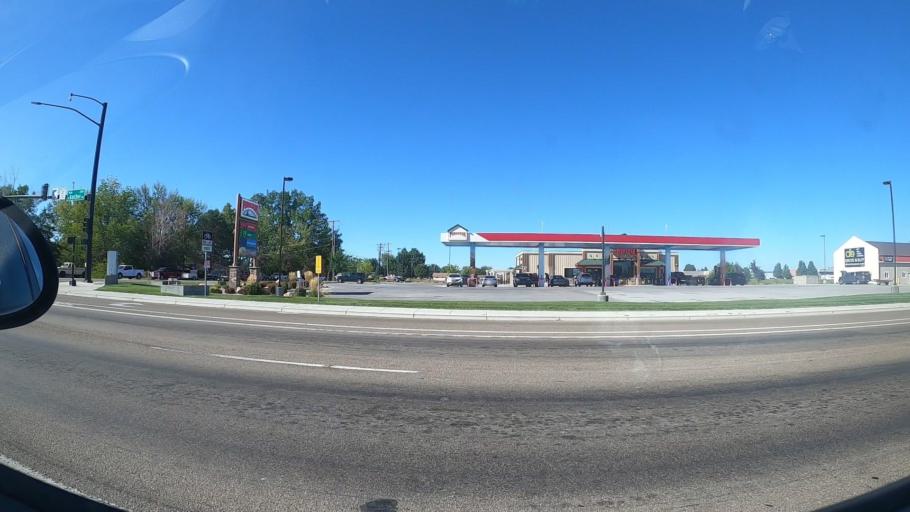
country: US
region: Idaho
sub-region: Canyon County
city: Nampa
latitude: 43.6050
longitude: -116.6110
